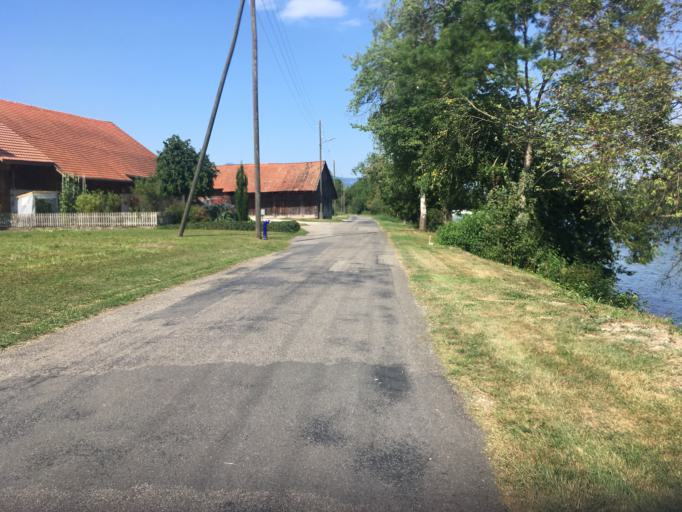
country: CH
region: Bern
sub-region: Biel/Bienne District
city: Meinisberg
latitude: 47.1449
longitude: 7.3819
